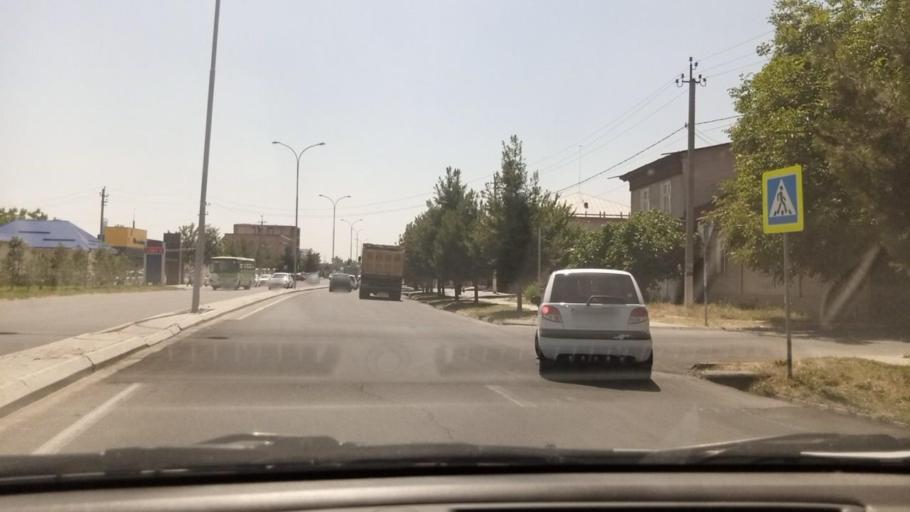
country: UZ
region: Toshkent Shahri
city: Tashkent
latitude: 41.2290
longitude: 69.1829
